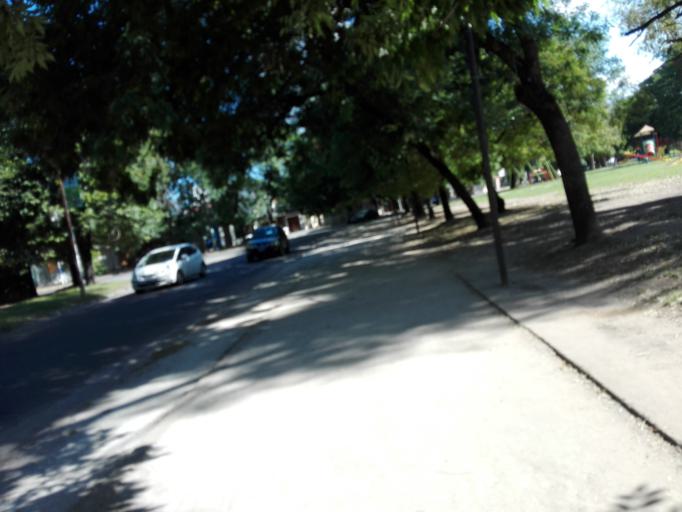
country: AR
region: Buenos Aires
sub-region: Partido de La Plata
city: La Plata
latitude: -34.9317
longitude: -57.9645
